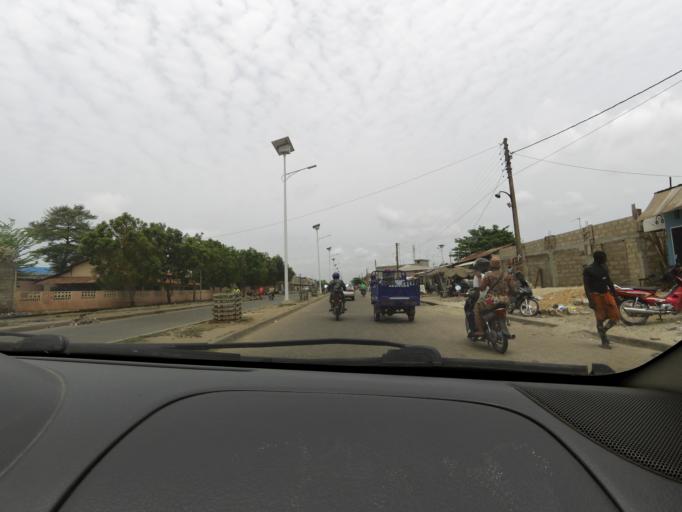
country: BJ
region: Littoral
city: Cotonou
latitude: 6.3566
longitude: 2.4238
